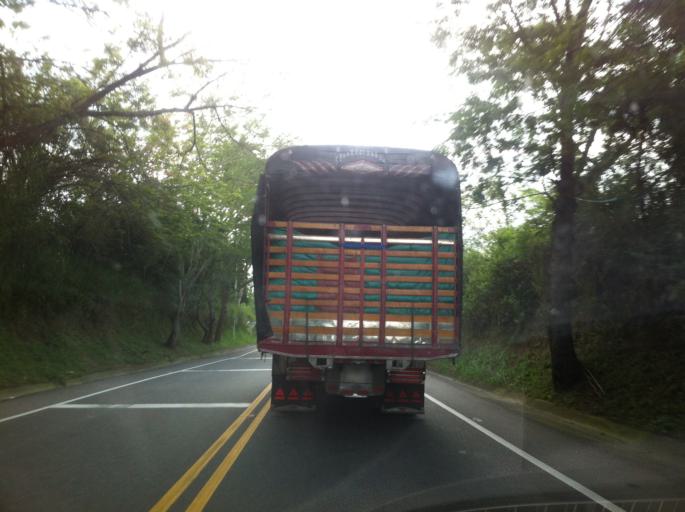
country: CO
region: Quindio
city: La Tebaida
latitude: 4.4471
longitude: -75.8249
